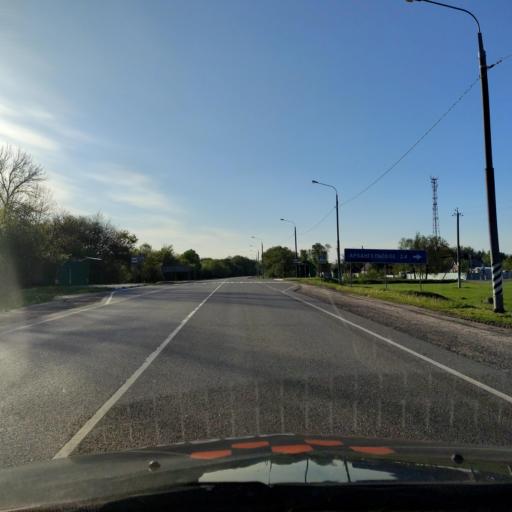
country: RU
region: Lipetsk
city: Yelets
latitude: 52.5819
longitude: 38.6308
